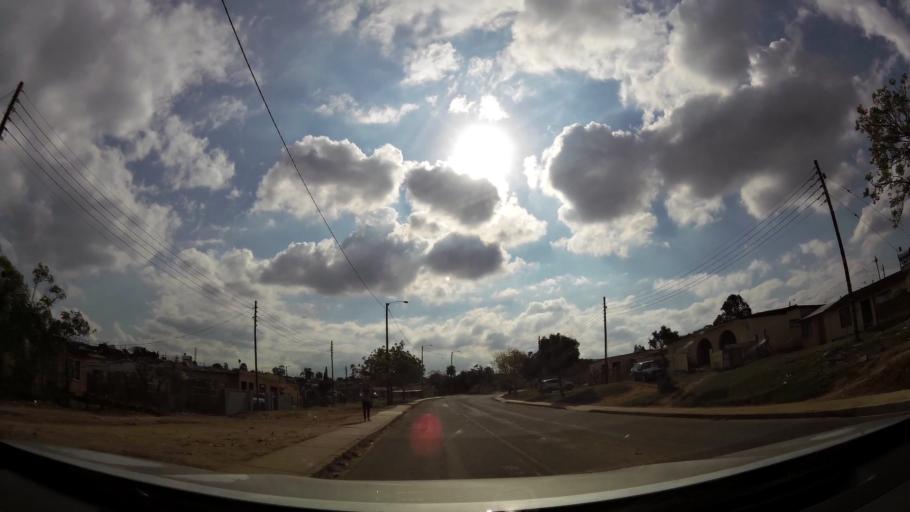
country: ZA
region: Eastern Cape
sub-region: Nelson Mandela Bay Metropolitan Municipality
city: Uitenhage
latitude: -33.7390
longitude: 25.3819
